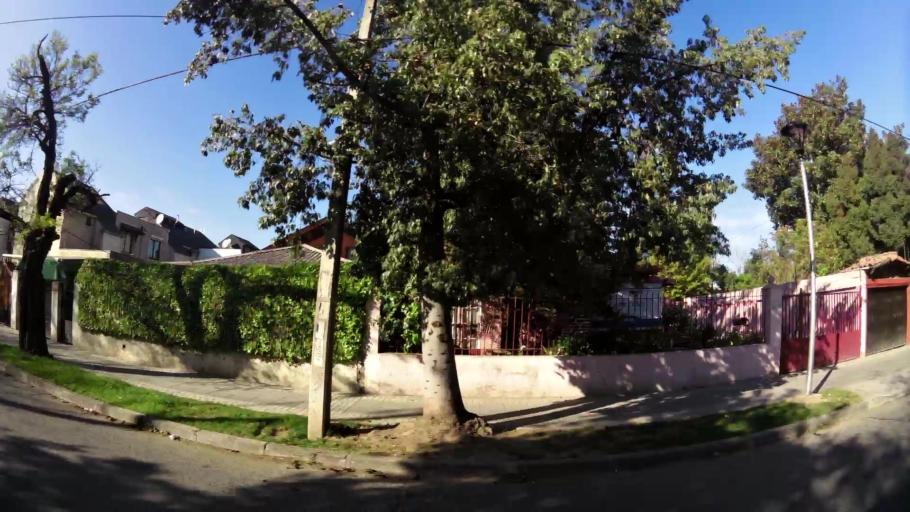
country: CL
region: Santiago Metropolitan
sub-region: Provincia de Santiago
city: Villa Presidente Frei, Nunoa, Santiago, Chile
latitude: -33.4586
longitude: -70.5679
